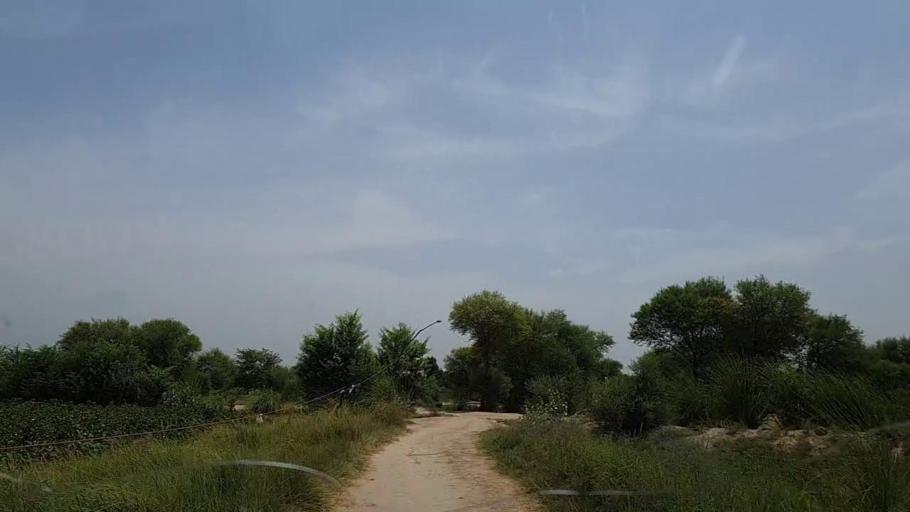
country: PK
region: Sindh
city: Khanpur
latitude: 27.7858
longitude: 69.4969
